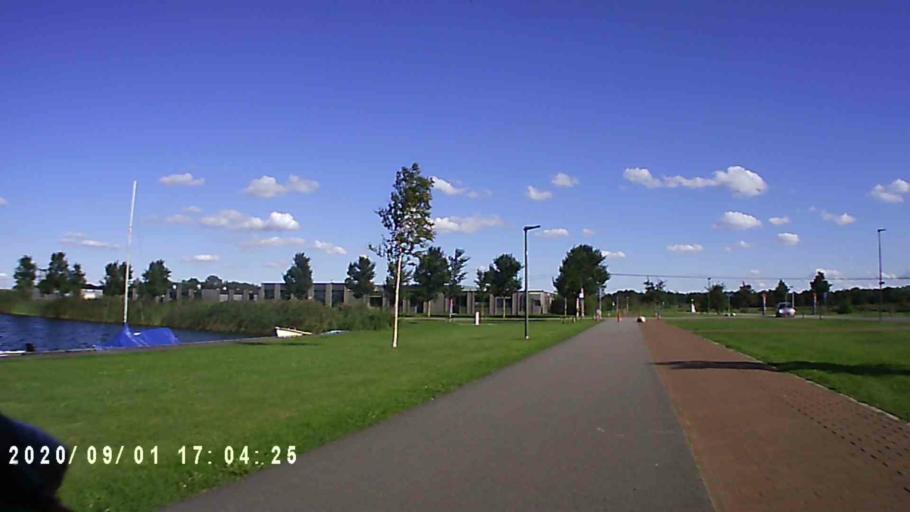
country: NL
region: Groningen
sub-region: Gemeente Haren
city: Haren
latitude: 53.2201
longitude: 6.6549
